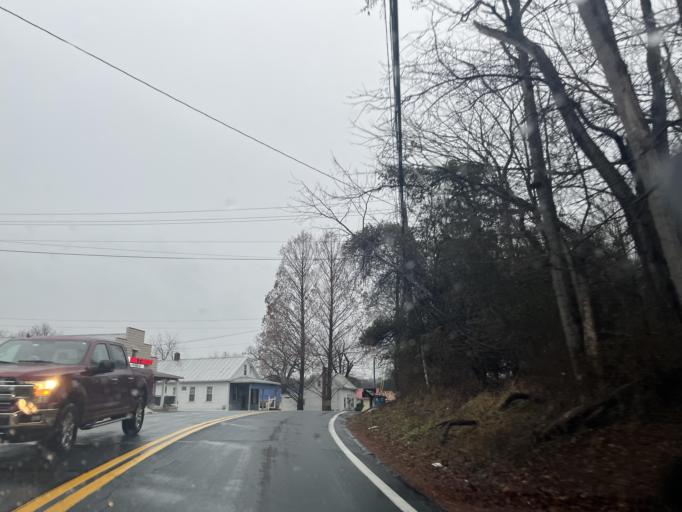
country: US
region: Maryland
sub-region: Montgomery County
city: Germantown
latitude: 39.1847
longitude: -77.3138
